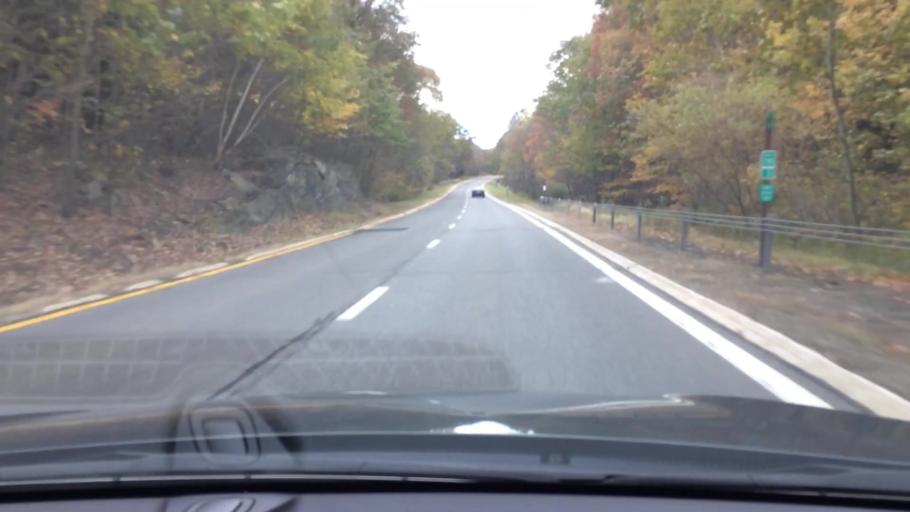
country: US
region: New York
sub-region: Dutchess County
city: Pine Plains
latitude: 42.0542
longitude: -73.7314
